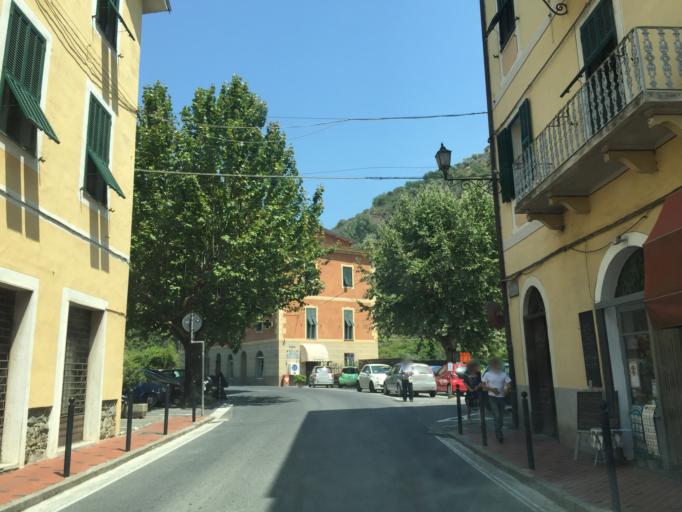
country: IT
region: Liguria
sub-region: Provincia di Imperia
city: Dolceacqua
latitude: 43.8525
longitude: 7.6241
